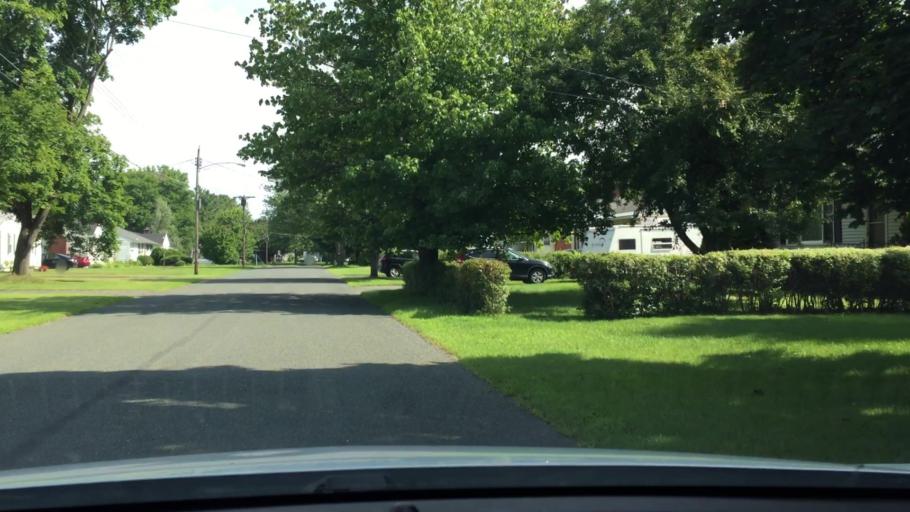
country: US
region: Massachusetts
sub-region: Berkshire County
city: Pittsfield
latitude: 42.4326
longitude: -73.2127
